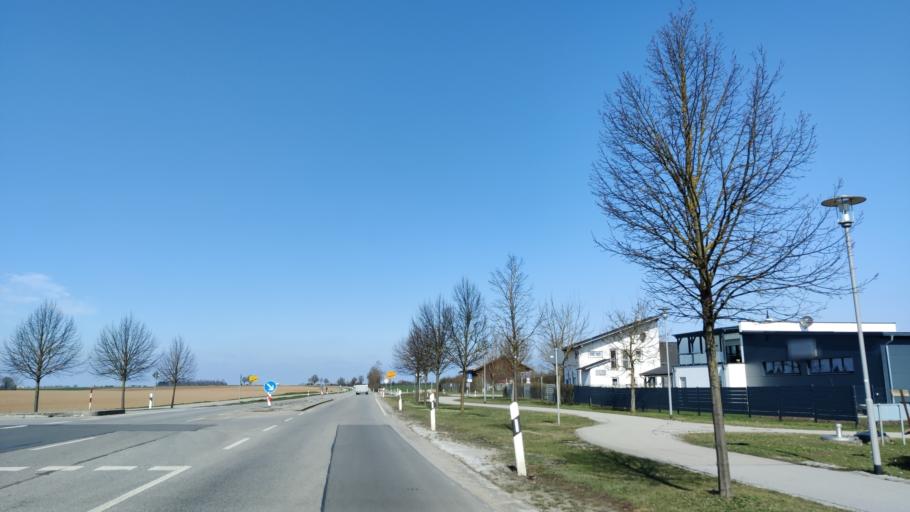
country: DE
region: Bavaria
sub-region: Lower Bavaria
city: Strasskirchen
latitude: 48.8351
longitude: 12.7098
